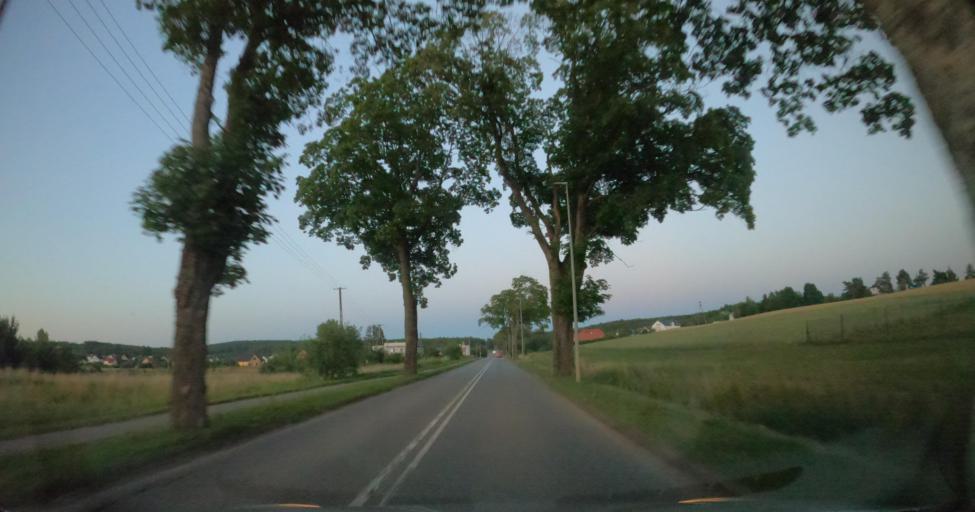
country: PL
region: Pomeranian Voivodeship
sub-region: Powiat wejherowski
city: Szemud
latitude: 54.4853
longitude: 18.2340
